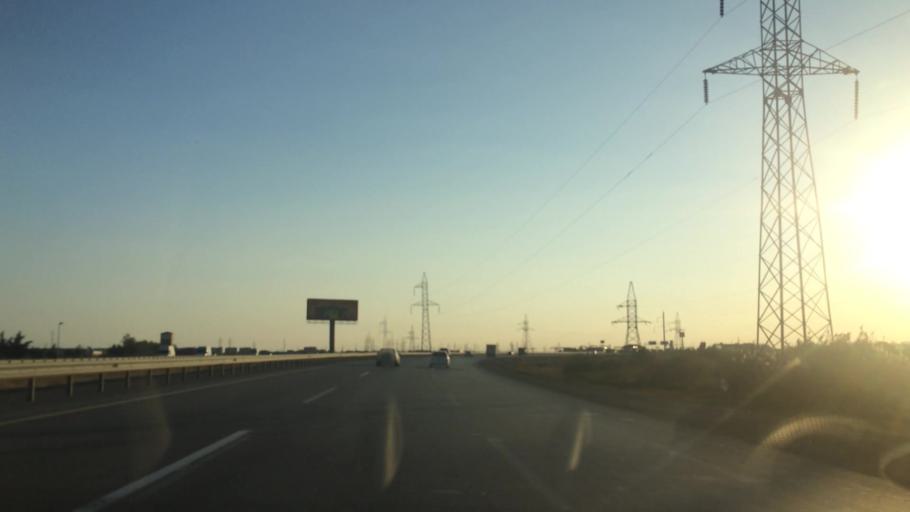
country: AZ
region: Baki
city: Qobustan
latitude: 39.9706
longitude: 49.4143
